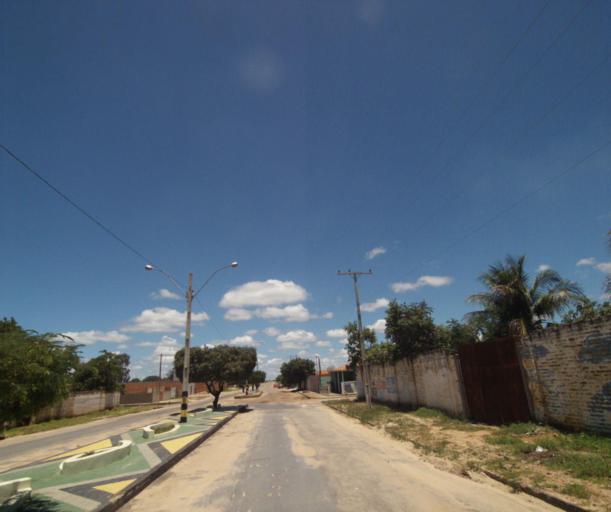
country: BR
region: Bahia
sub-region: Carinhanha
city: Carinhanha
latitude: -14.2950
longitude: -43.7747
